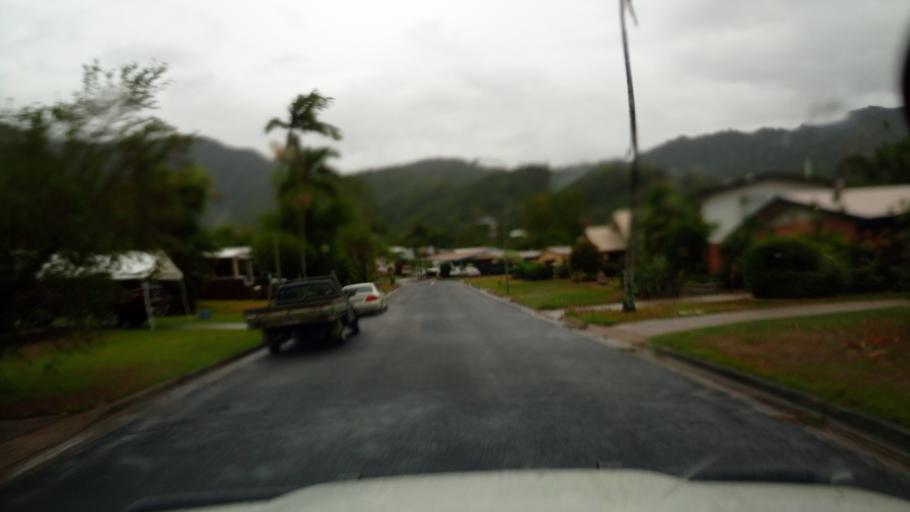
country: AU
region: Queensland
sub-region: Cairns
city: Woree
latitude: -16.9555
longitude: 145.7312
